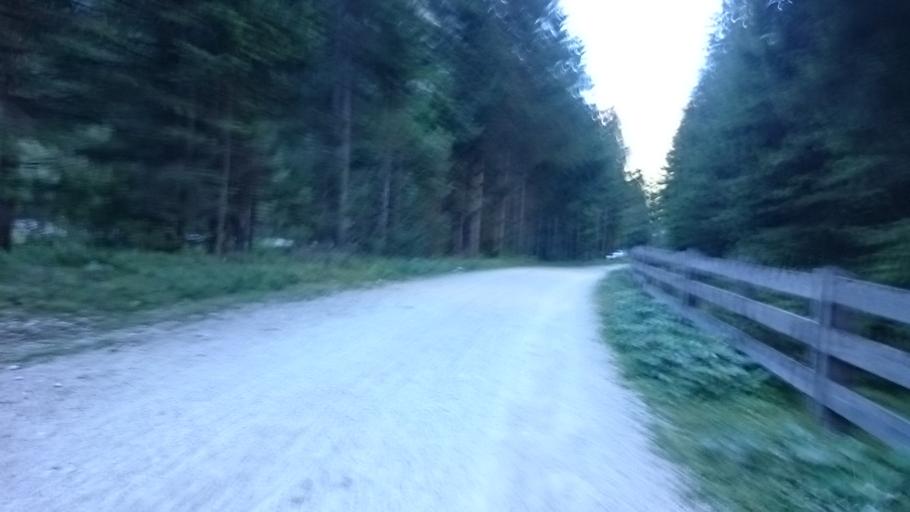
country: IT
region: Trentino-Alto Adige
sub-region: Bolzano
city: Dobbiaco
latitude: 46.6826
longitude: 12.2242
